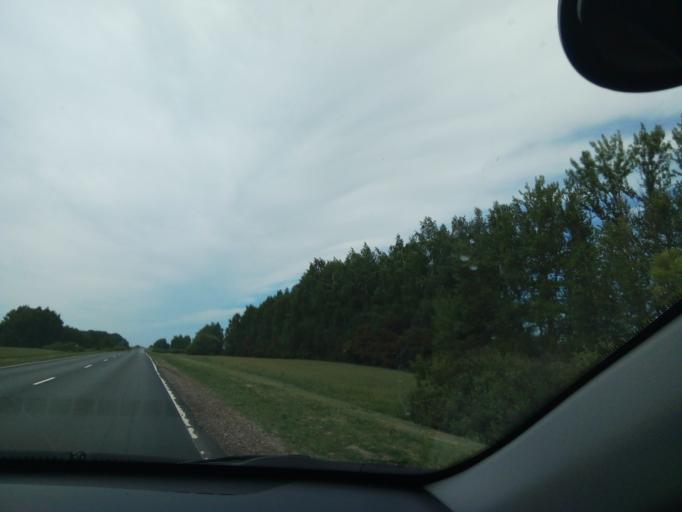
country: RU
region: Tambov
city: Selezni
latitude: 52.6424
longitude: 40.9769
